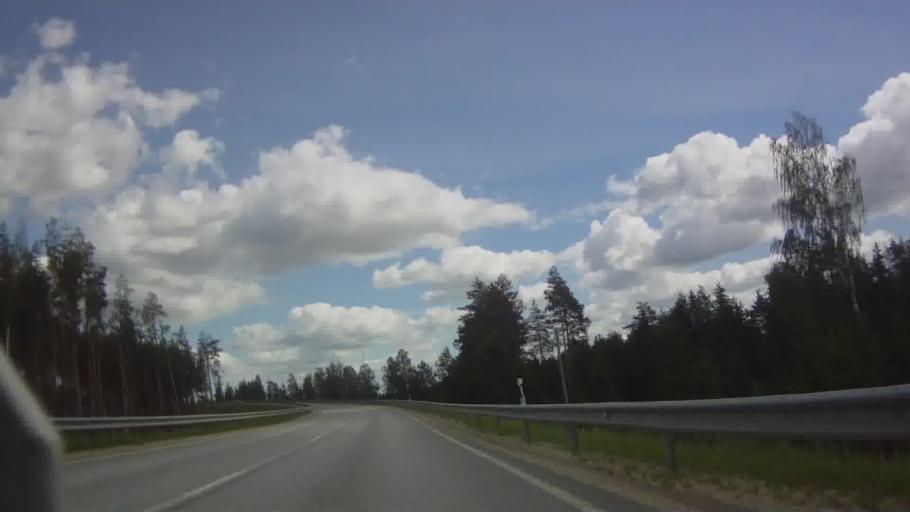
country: LV
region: Varaklani
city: Varaklani
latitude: 56.5278
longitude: 26.5265
